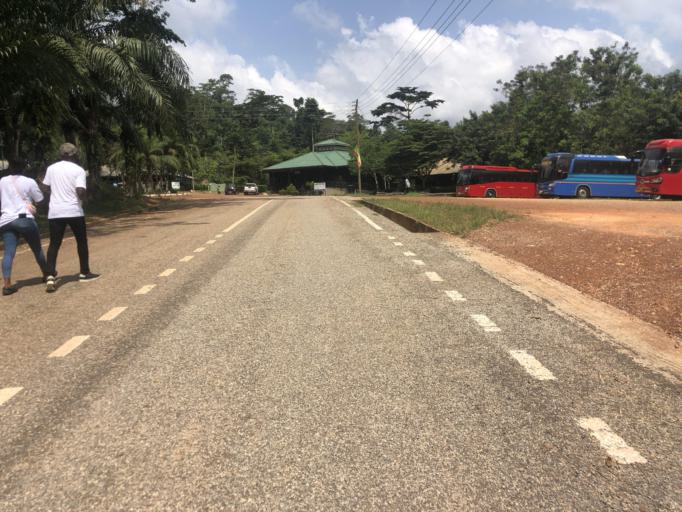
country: GH
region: Central
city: Elmina
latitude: 5.3478
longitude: -1.3832
